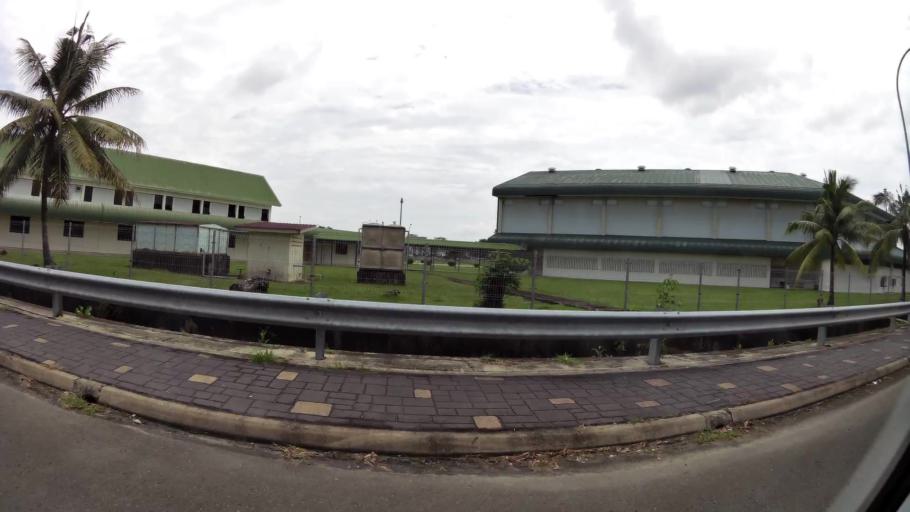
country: BN
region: Brunei and Muara
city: Bandar Seri Begawan
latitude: 4.9116
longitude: 114.9235
